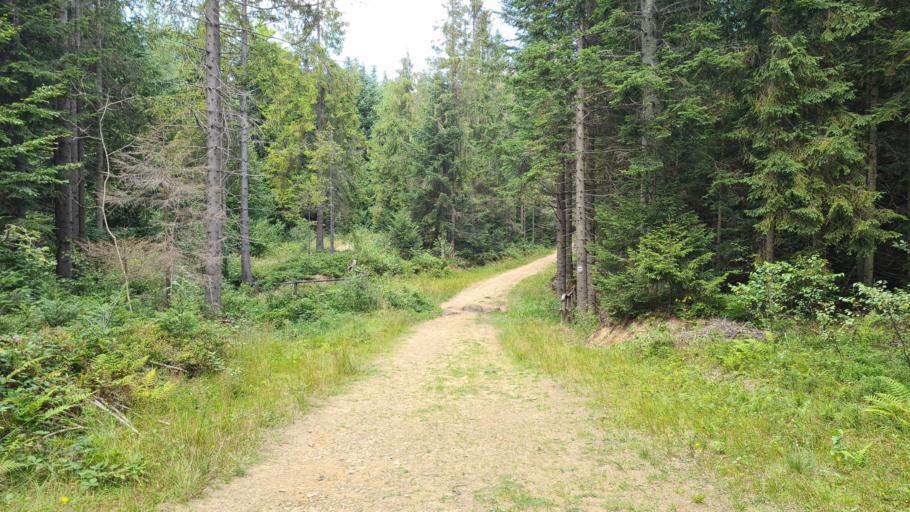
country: PL
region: Lesser Poland Voivodeship
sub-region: Powiat nowosadecki
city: Rytro
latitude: 49.4141
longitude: 20.6222
